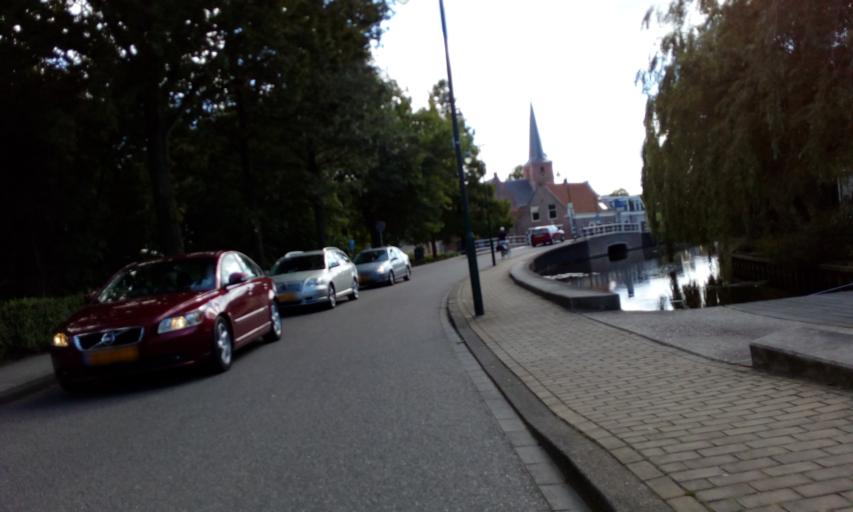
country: NL
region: South Holland
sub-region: Gemeente Leiden
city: Leiden
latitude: 52.1228
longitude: 4.4977
